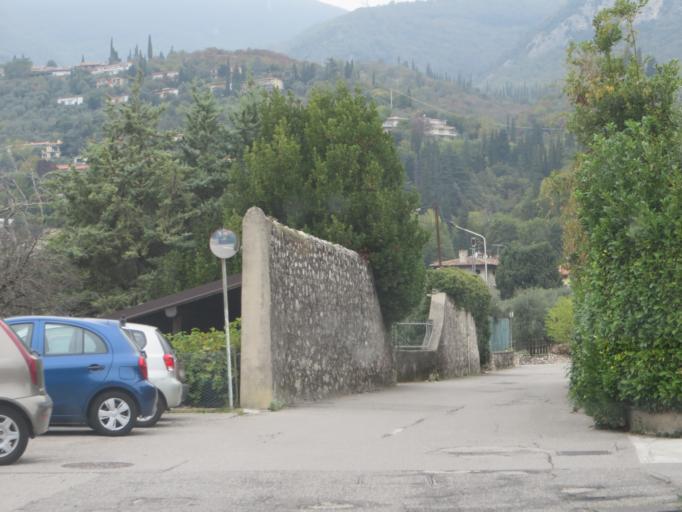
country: IT
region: Lombardy
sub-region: Provincia di Brescia
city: Toscolano Maderno
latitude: 45.6353
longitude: 10.6099
